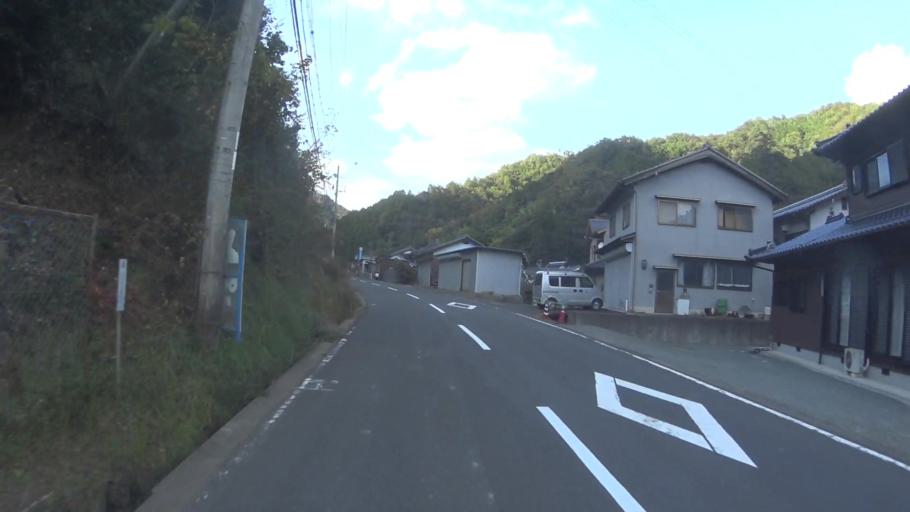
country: JP
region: Kyoto
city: Maizuru
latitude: 35.4594
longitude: 135.2596
